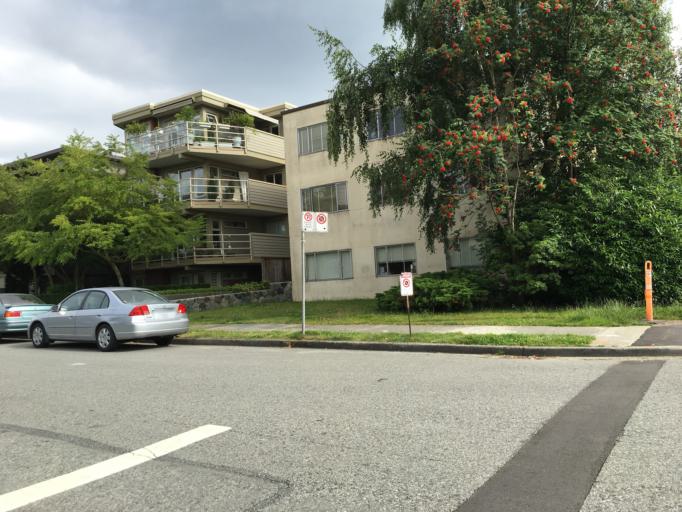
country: CA
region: British Columbia
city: West End
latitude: 49.2618
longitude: -123.1411
